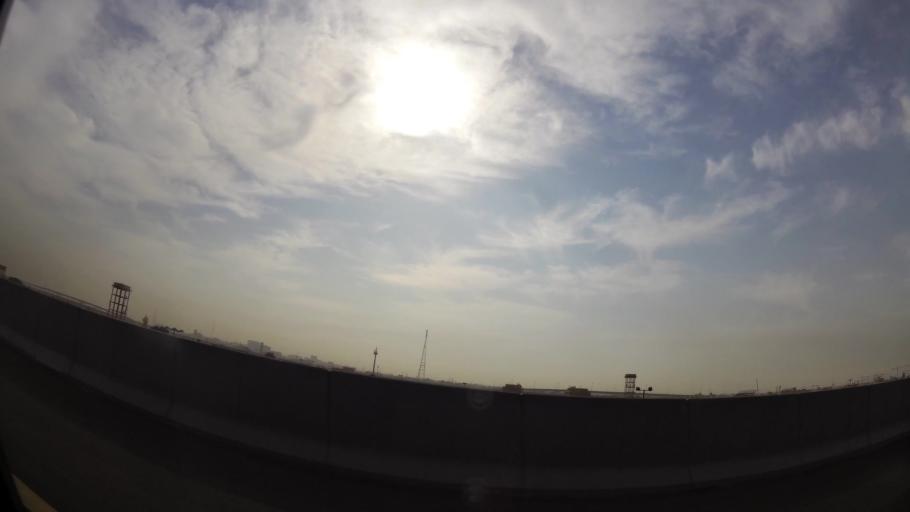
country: KW
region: Al Asimah
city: Ar Rabiyah
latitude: 29.3180
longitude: 47.8832
